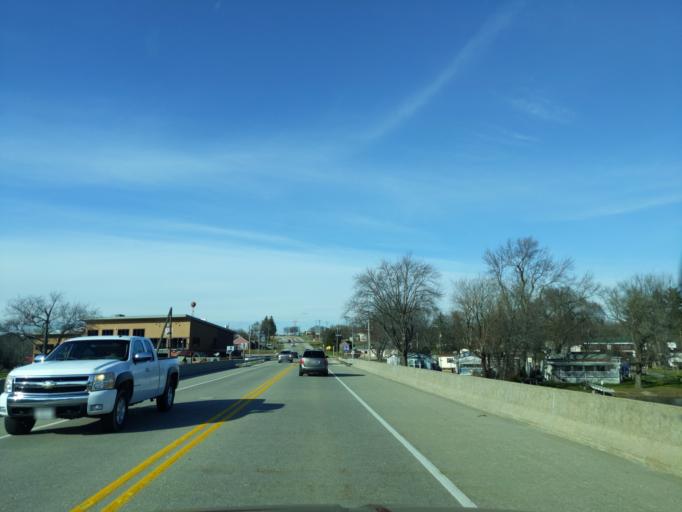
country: US
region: Wisconsin
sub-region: Rock County
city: Edgerton
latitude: 42.8299
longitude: -89.0211
